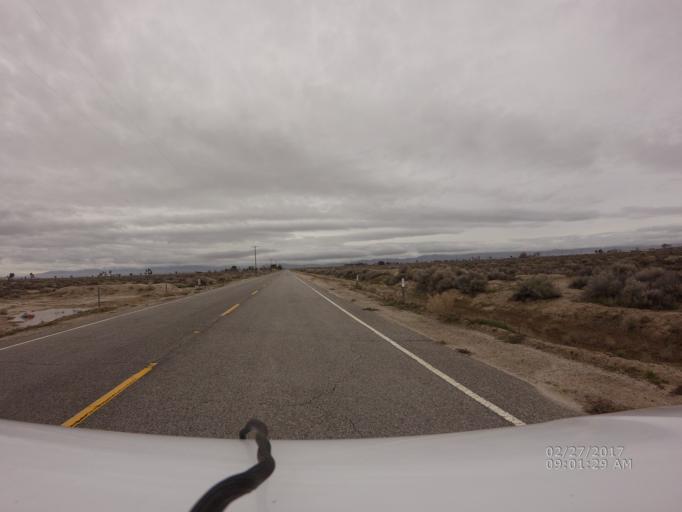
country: US
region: California
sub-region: Los Angeles County
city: Lancaster
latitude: 34.7592
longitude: -118.0773
